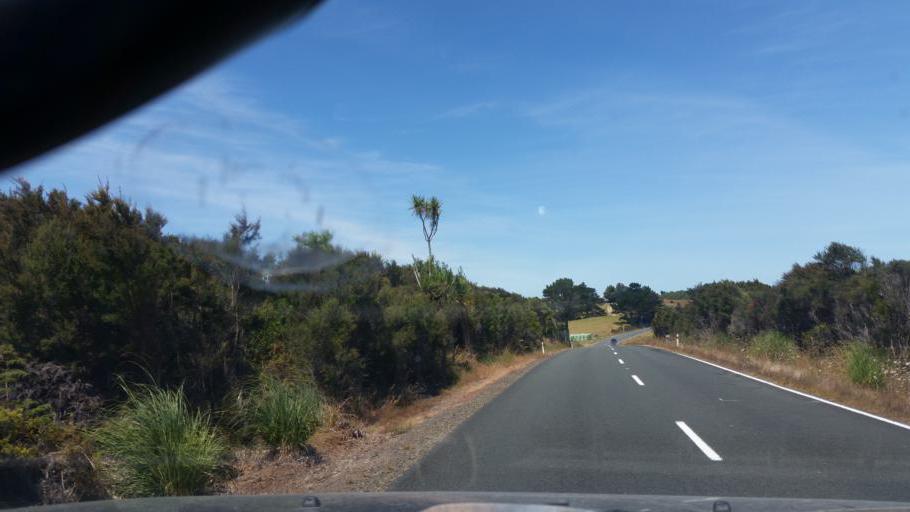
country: NZ
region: Auckland
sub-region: Auckland
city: Wellsford
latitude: -36.2078
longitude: 174.1783
